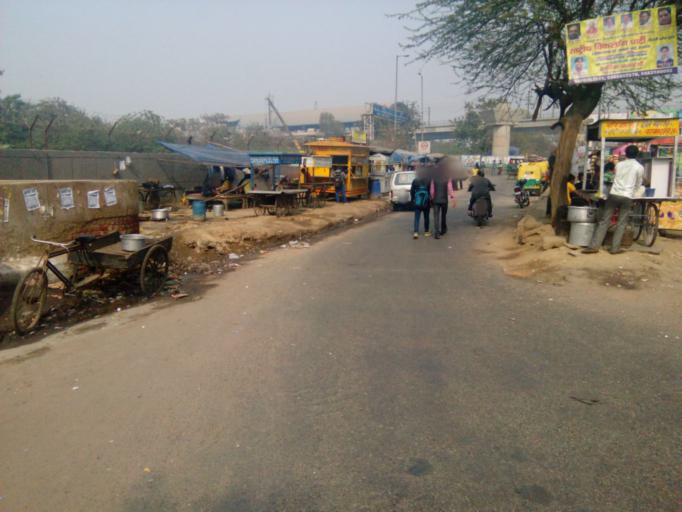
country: IN
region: Uttar Pradesh
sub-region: Gautam Buddha Nagar
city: Noida
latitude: 28.6449
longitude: 77.3168
